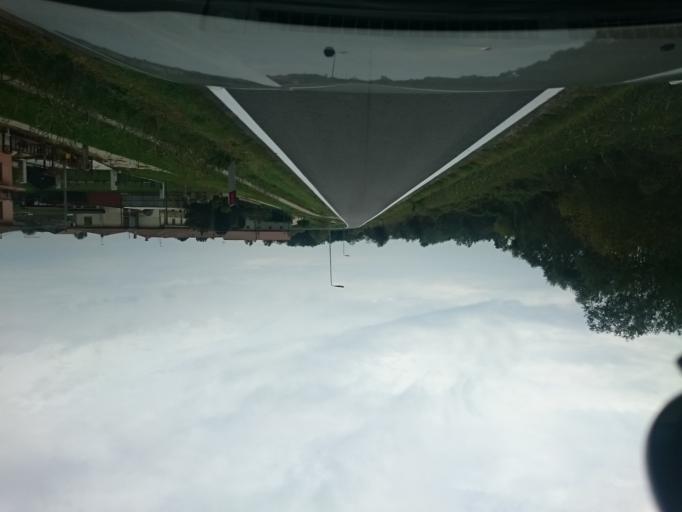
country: IT
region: Veneto
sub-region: Provincia di Padova
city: Correzzola
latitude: 45.2363
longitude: 12.0756
